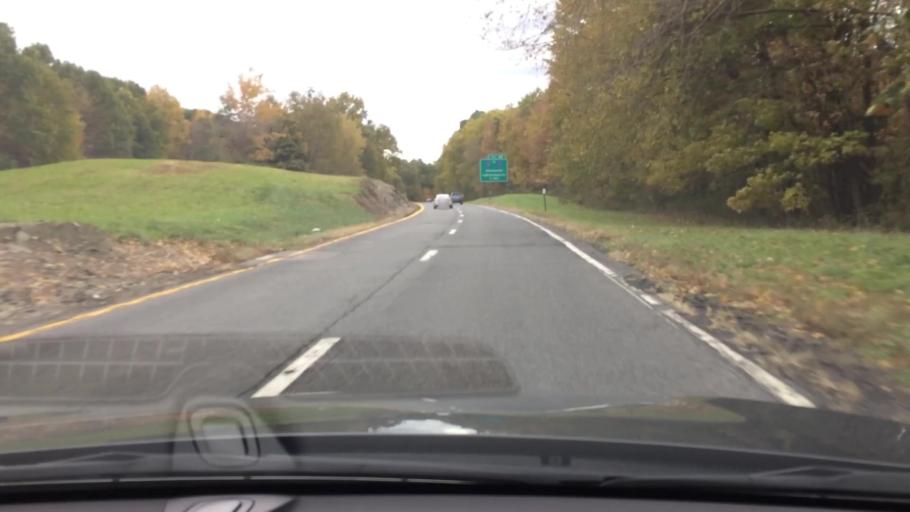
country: US
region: New York
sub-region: Dutchess County
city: Hillside Lake
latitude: 41.6411
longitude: -73.7867
